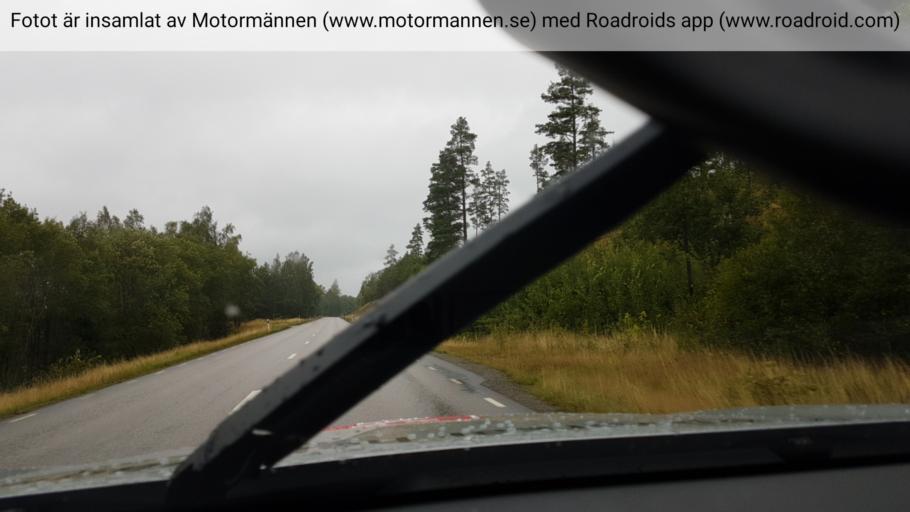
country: SE
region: Vaestra Goetaland
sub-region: Bengtsfors Kommun
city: Billingsfors
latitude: 58.9199
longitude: 12.2222
